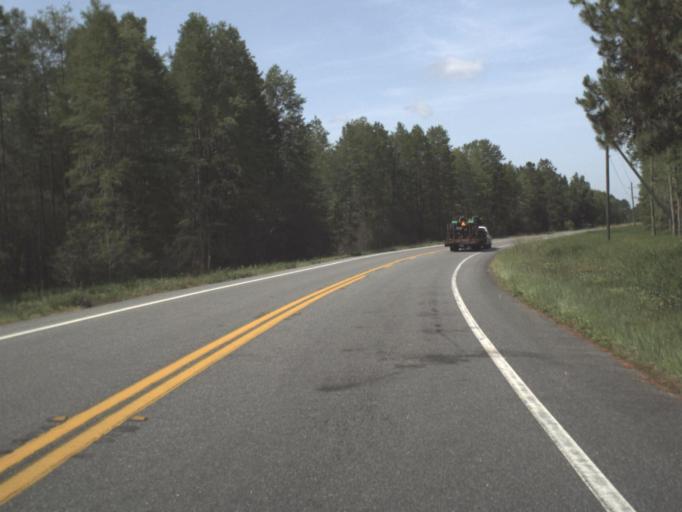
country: US
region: Florida
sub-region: Lafayette County
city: Mayo
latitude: 30.0409
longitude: -83.1756
